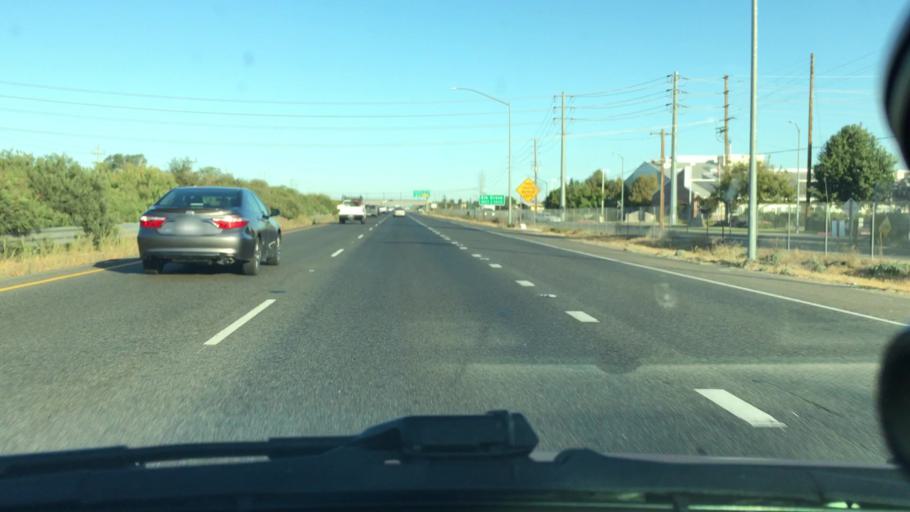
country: US
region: California
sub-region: Sacramento County
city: Elk Grove
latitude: 38.3703
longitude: -121.3558
